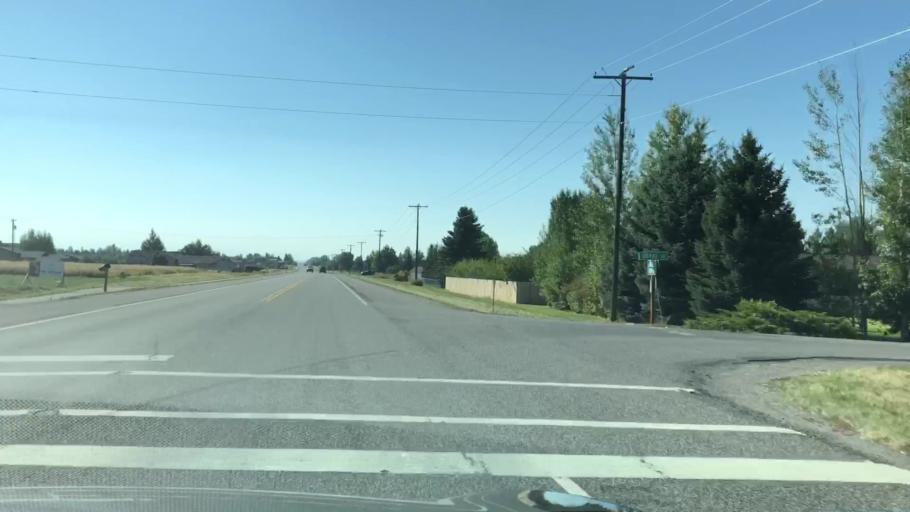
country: US
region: Montana
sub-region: Gallatin County
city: Belgrade
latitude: 45.7293
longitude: -111.1214
